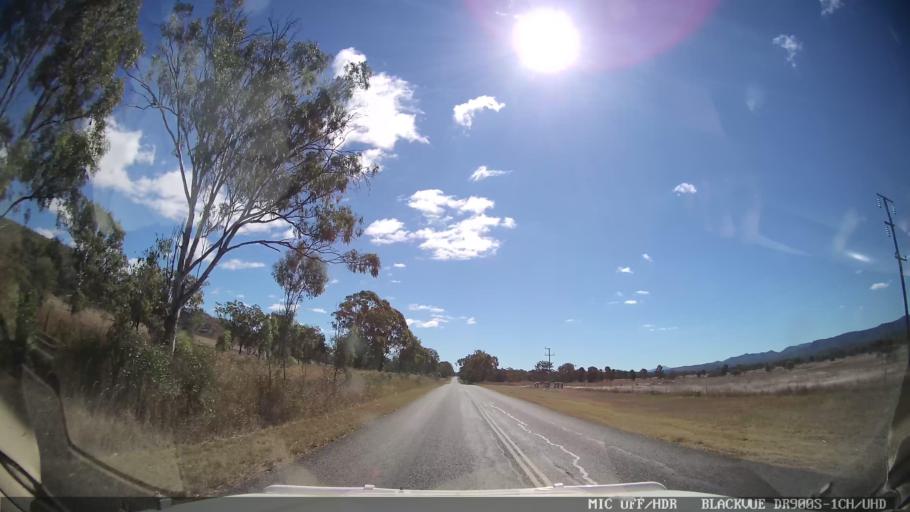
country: AU
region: Queensland
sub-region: Gladstone
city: Toolooa
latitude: -24.4500
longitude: 151.3450
